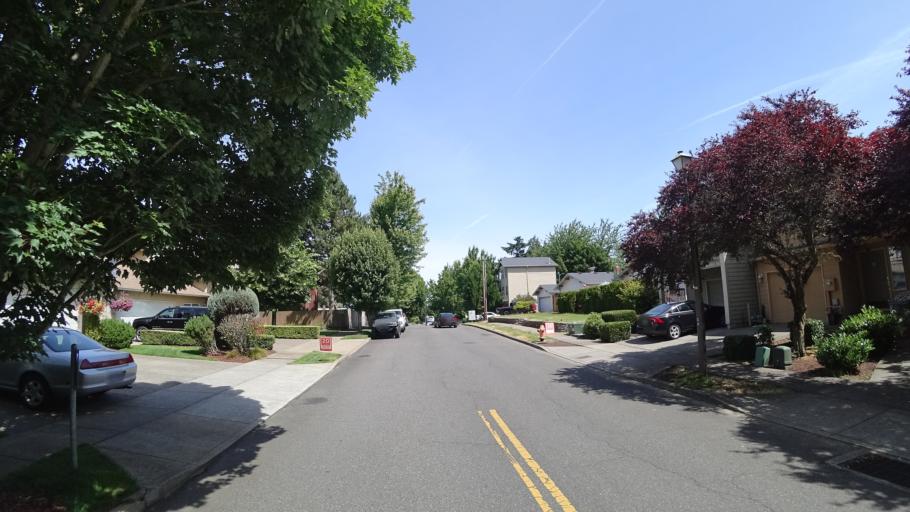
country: US
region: Oregon
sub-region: Multnomah County
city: Fairview
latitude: 45.5484
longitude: -122.5040
